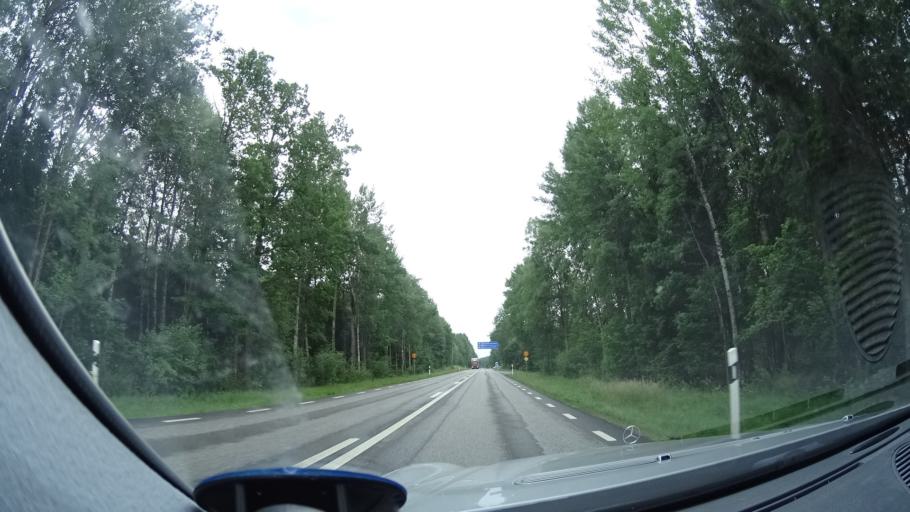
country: SE
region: Kronoberg
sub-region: Tingsryds Kommun
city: Tingsryd
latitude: 56.4703
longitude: 15.0090
